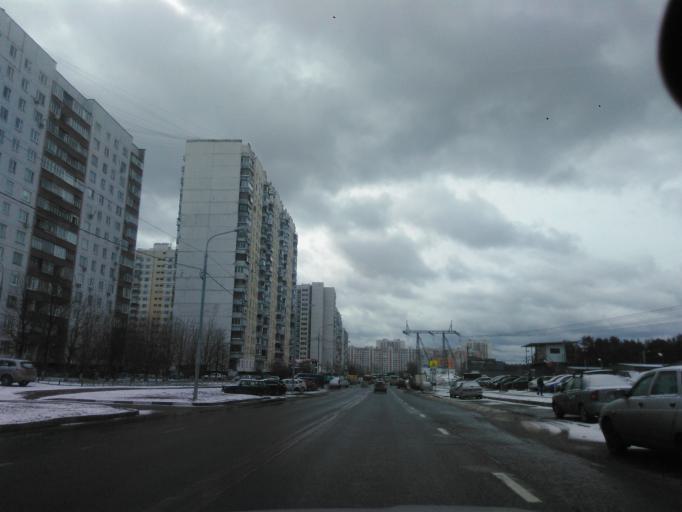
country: RU
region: Moskovskaya
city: Krasnogorsk
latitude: 55.8551
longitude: 37.3422
